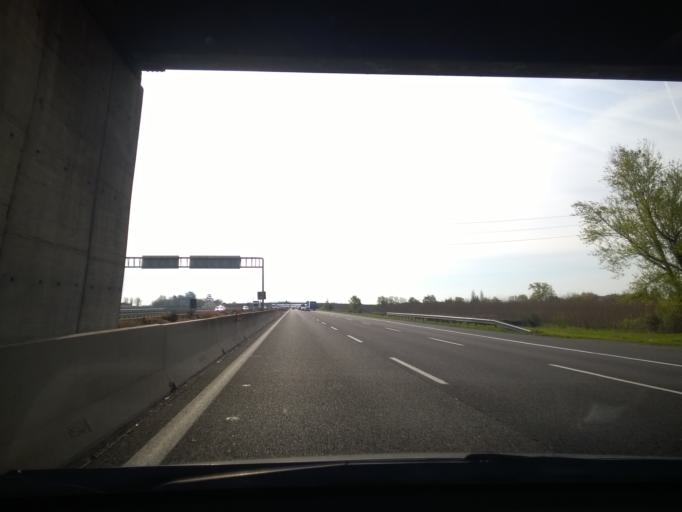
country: IT
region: Emilia-Romagna
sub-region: Provincia di Bologna
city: Imola
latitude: 44.3788
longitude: 11.7473
